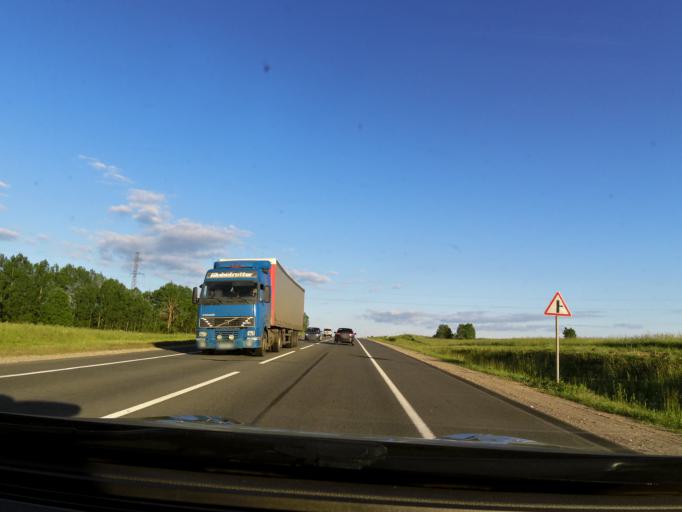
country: RU
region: Vologda
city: Vologda
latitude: 59.1122
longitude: 39.9793
